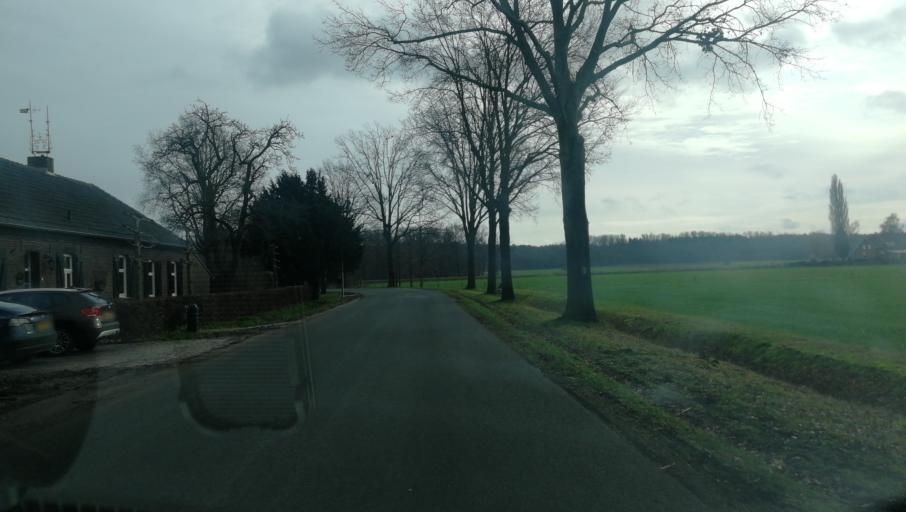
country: NL
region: Limburg
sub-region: Gemeente Beesel
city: Offenbeek
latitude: 51.2998
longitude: 6.1302
